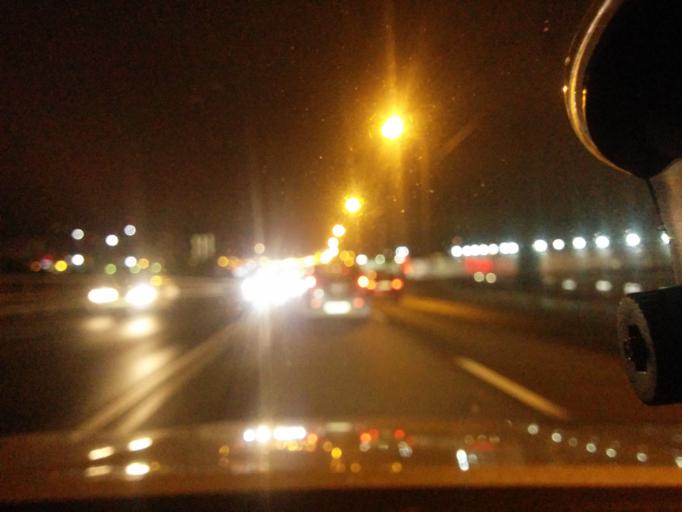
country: RU
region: Leningrad
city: Parnas
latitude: 60.0618
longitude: 30.3417
